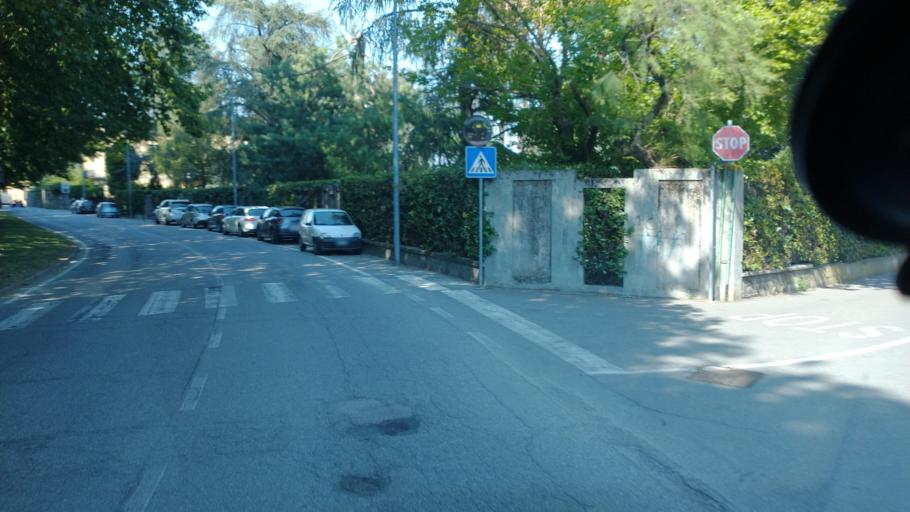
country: IT
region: Lombardy
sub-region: Provincia di Bergamo
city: Cologno al Serio
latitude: 45.5779
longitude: 9.7104
